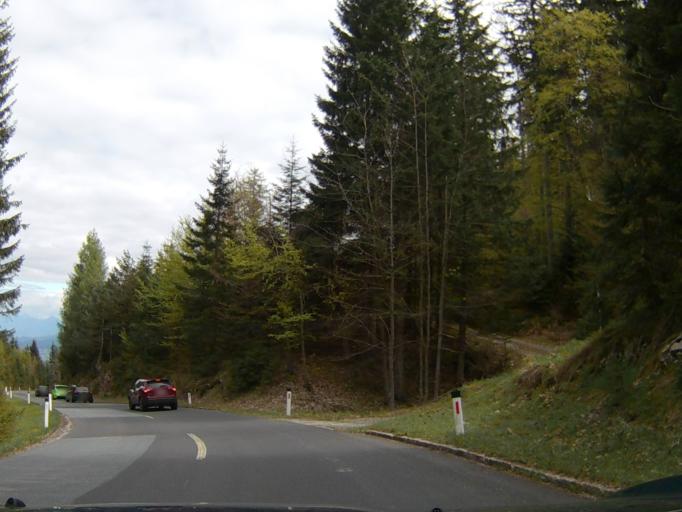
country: AT
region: Carinthia
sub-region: Politischer Bezirk Villach Land
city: Arnoldstein
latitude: 46.5927
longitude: 13.7695
